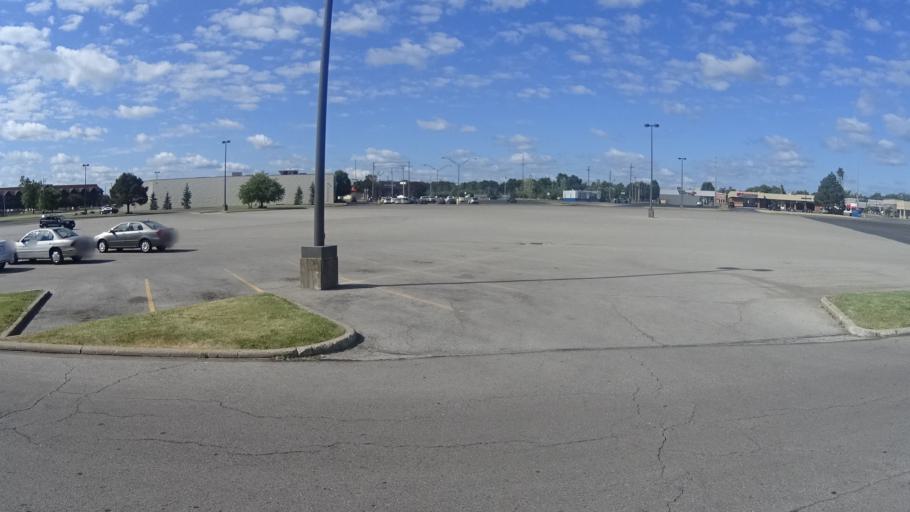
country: US
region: Ohio
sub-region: Erie County
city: Sandusky
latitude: 41.4170
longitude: -82.6690
